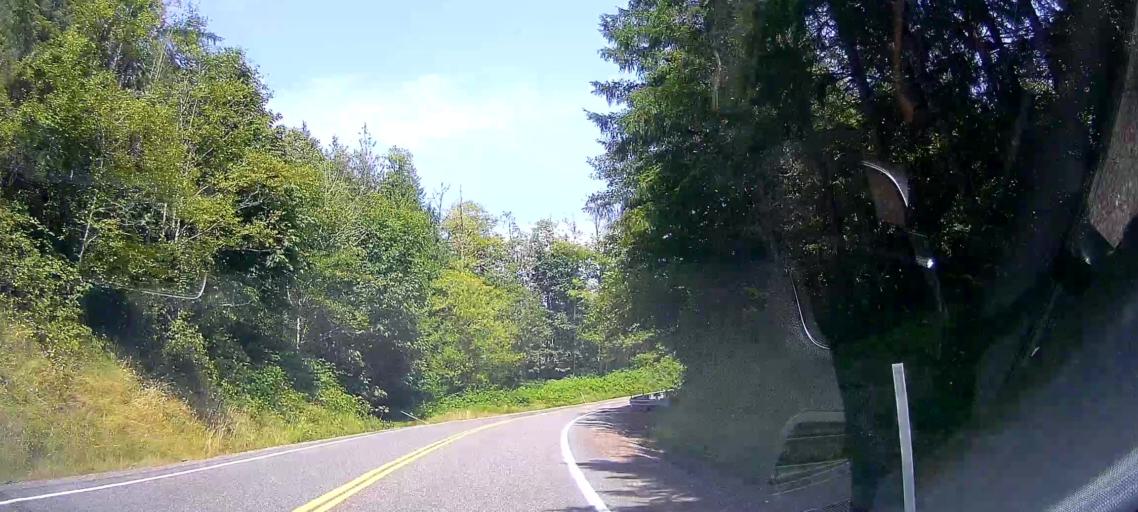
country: US
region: Washington
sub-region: Snohomish County
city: Bryant
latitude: 48.3391
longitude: -122.1200
